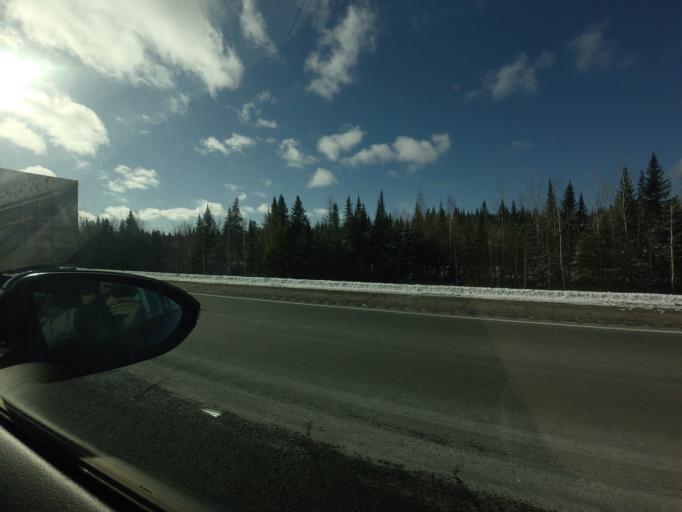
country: CA
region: New Brunswick
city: Fredericton
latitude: 45.8804
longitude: -66.6365
